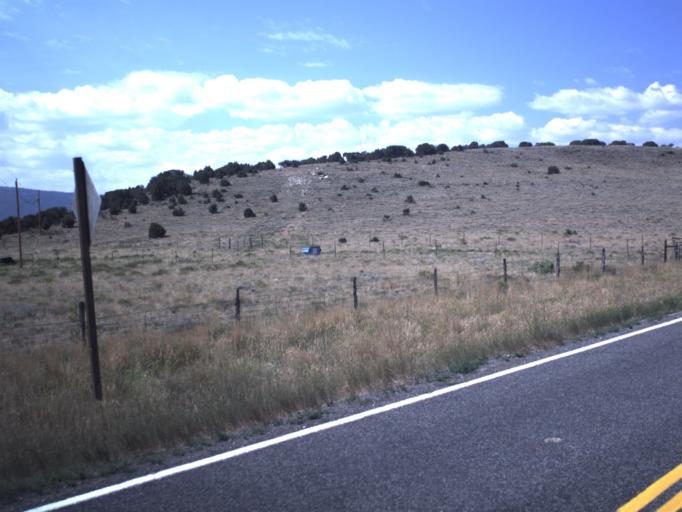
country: US
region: Utah
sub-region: Daggett County
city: Manila
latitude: 40.9762
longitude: -109.8262
